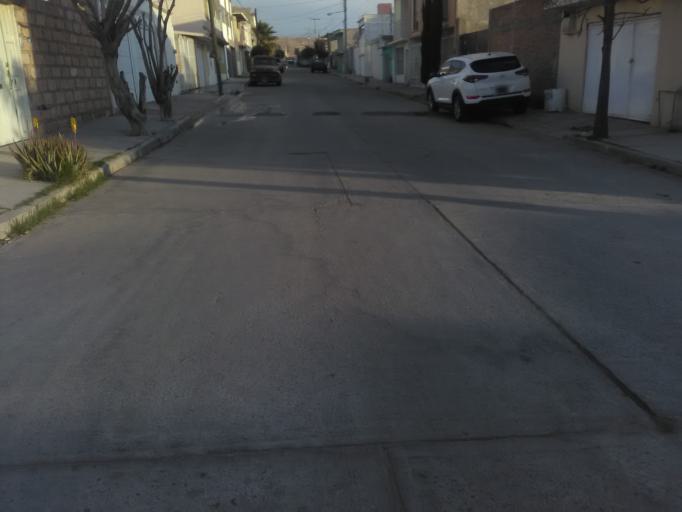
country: MX
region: Durango
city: Victoria de Durango
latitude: 24.0405
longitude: -104.6635
